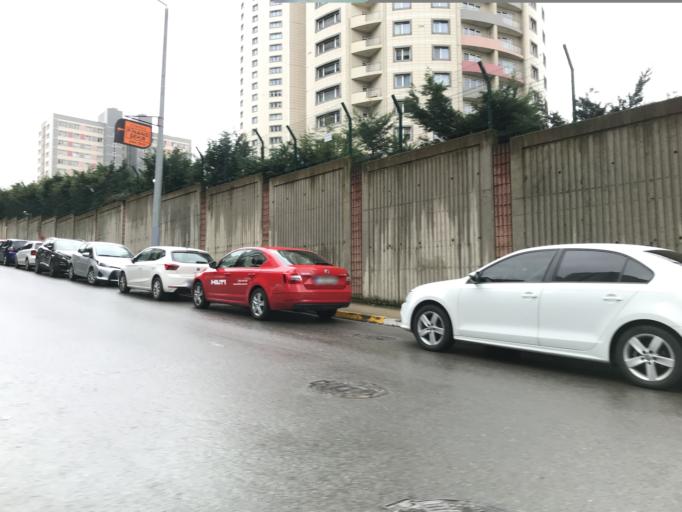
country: TR
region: Istanbul
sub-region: Atasehir
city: Atasehir
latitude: 40.9894
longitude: 29.1056
